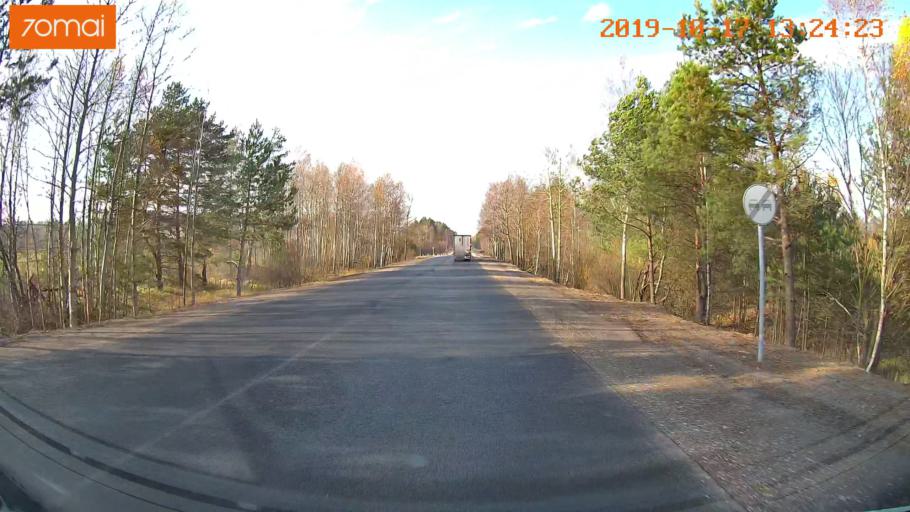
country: RU
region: Rjazan
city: Gus'-Zheleznyy
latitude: 55.0951
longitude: 40.9640
